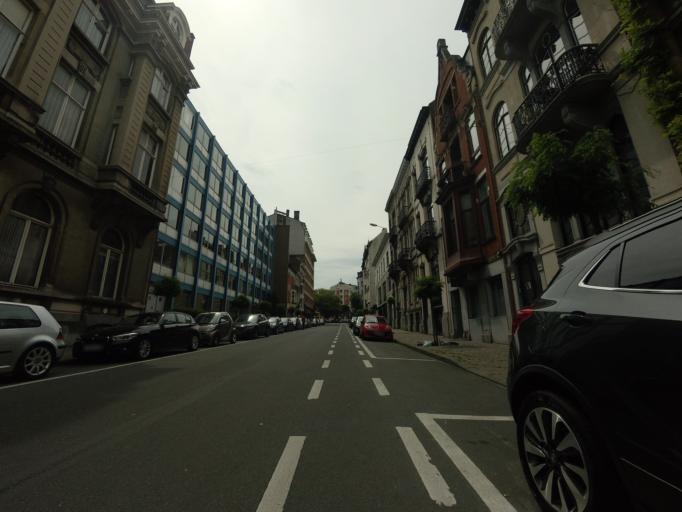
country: BE
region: Brussels Capital
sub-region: Bruxelles-Capitale
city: Brussels
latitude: 50.8195
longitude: 4.3630
